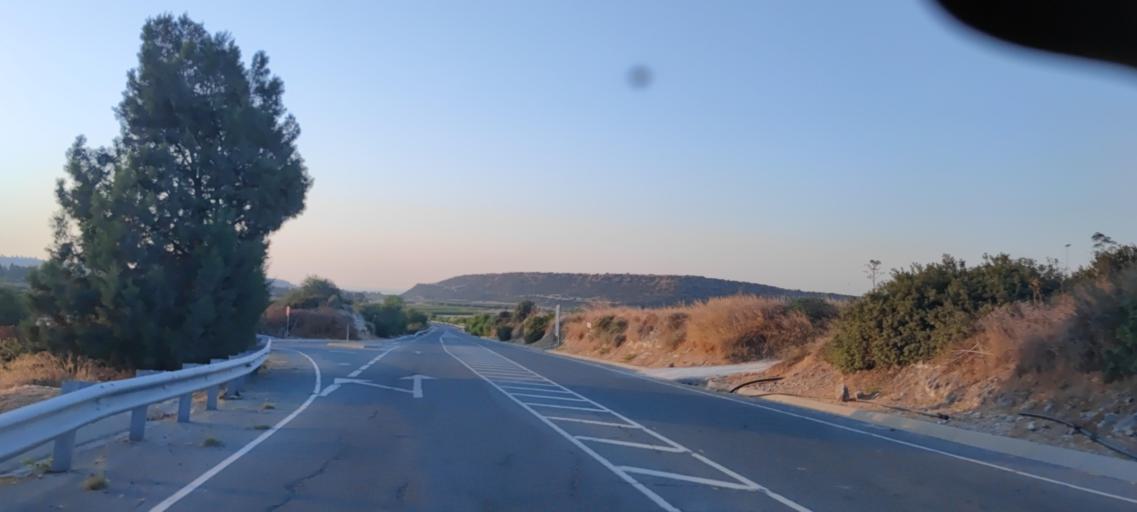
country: CY
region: Limassol
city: Pissouri
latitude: 34.6809
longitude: 32.7691
